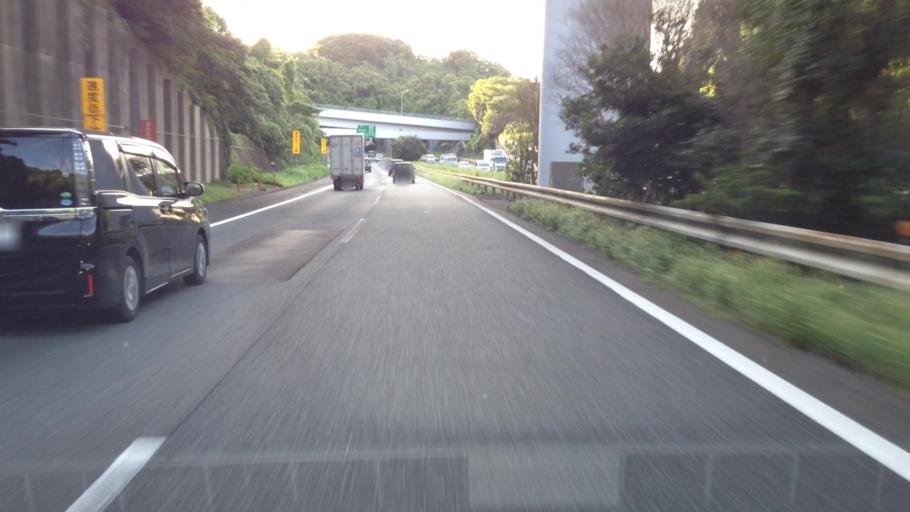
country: JP
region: Kanagawa
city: Zushi
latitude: 35.3240
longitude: 139.6009
